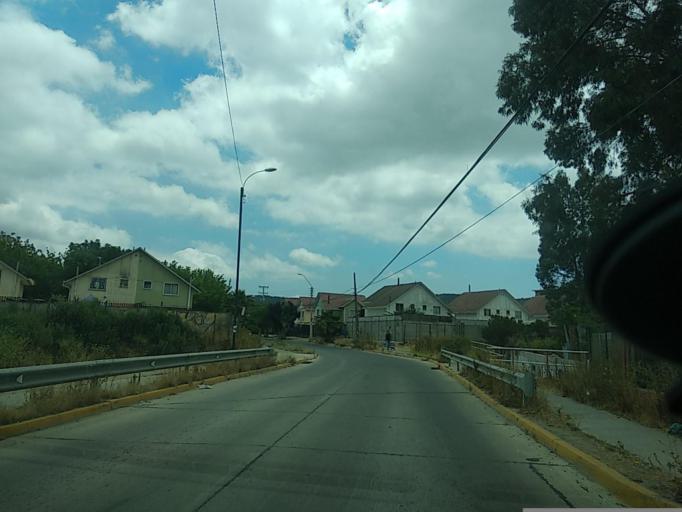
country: CL
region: Valparaiso
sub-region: Provincia de Marga Marga
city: Villa Alemana
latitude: -33.0334
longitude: -71.4057
